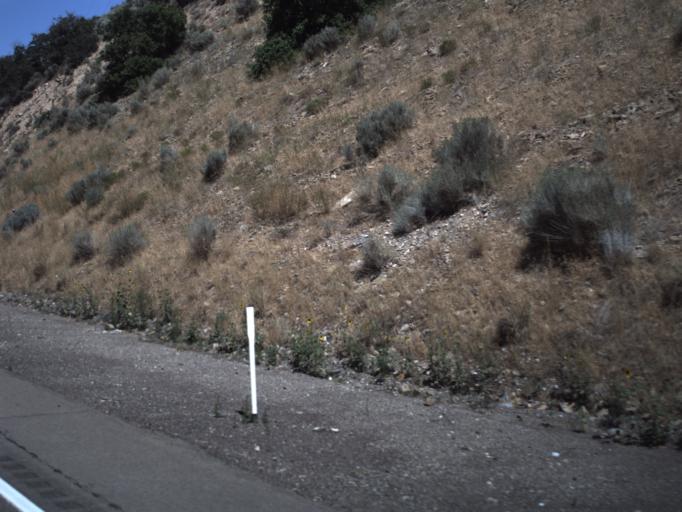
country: US
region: Utah
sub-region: Utah County
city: Mapleton
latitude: 40.0601
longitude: -111.5675
